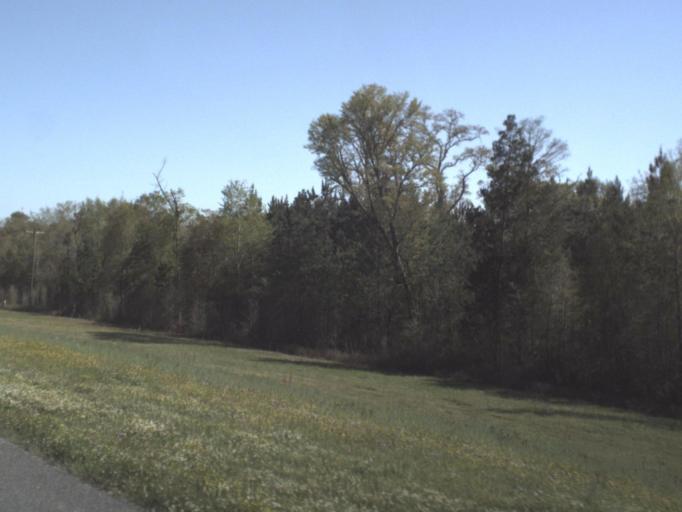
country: US
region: Florida
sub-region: Holmes County
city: Bonifay
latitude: 30.7732
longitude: -85.8217
